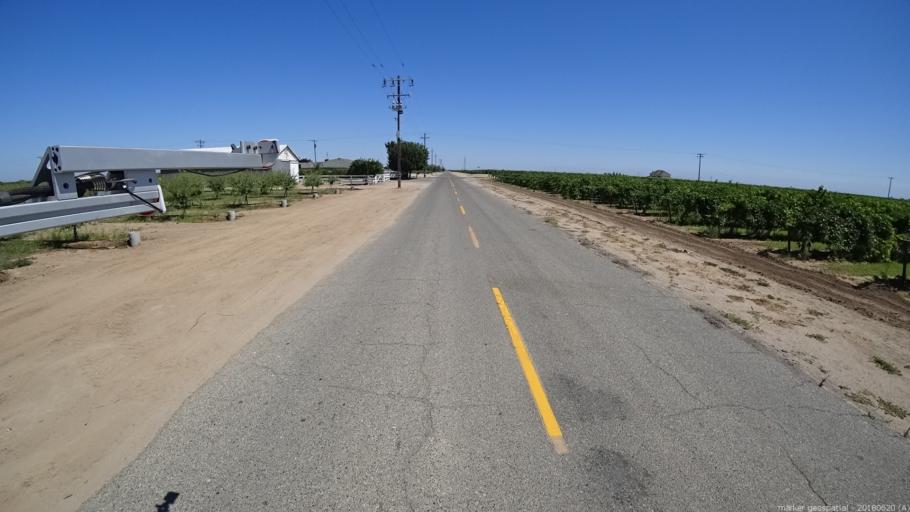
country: US
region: California
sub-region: Fresno County
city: Biola
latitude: 36.8650
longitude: -120.0014
